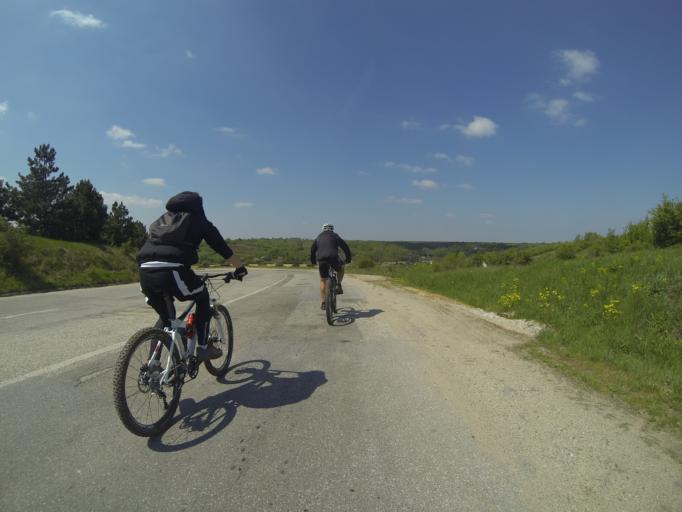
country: RO
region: Dolj
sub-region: Comuna Terpezita
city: Terpezita
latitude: 44.2935
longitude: 23.5469
